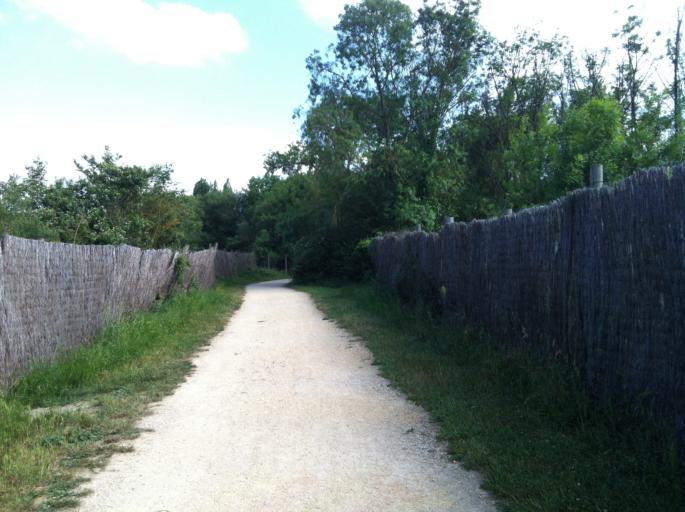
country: ES
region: Basque Country
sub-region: Provincia de Alava
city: Gasteiz / Vitoria
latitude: 42.8576
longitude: -2.6328
